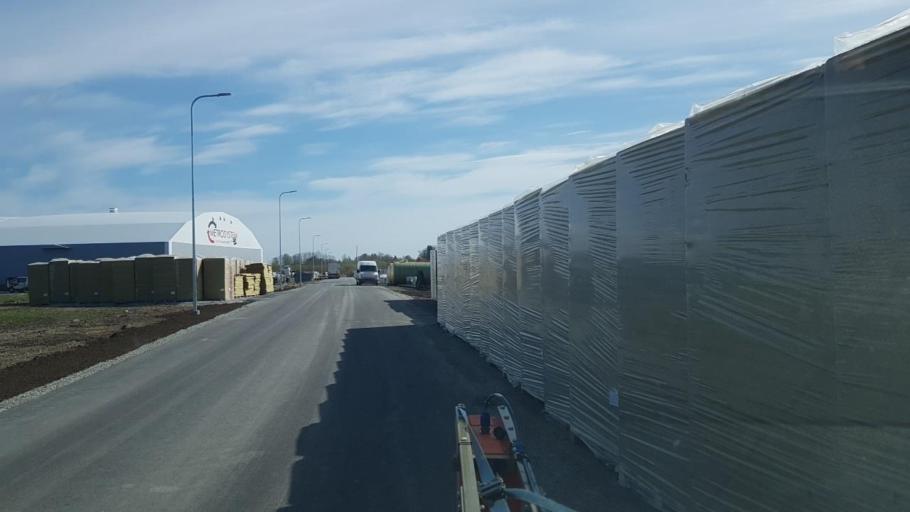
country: EE
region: Harju
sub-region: Kiili vald
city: Kiili
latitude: 59.3342
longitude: 24.7983
